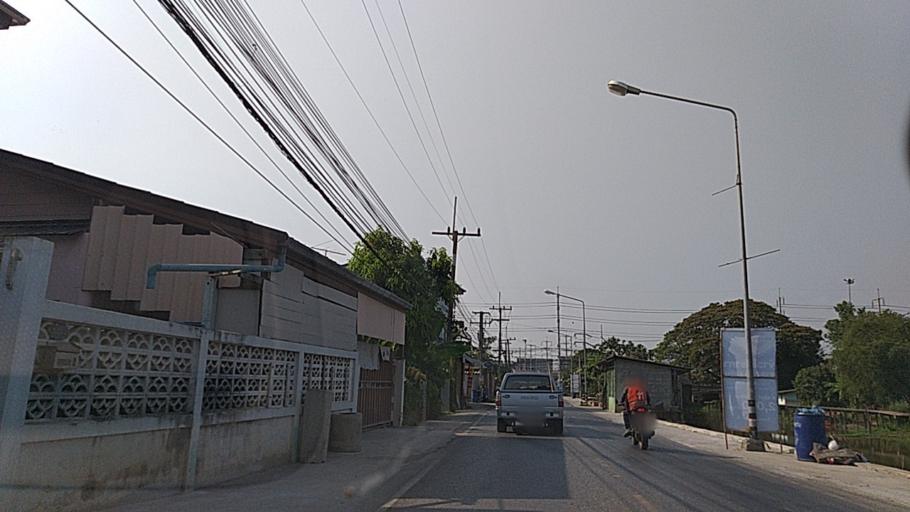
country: TH
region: Pathum Thani
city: Lam Luk Ka
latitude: 13.9348
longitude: 100.7062
